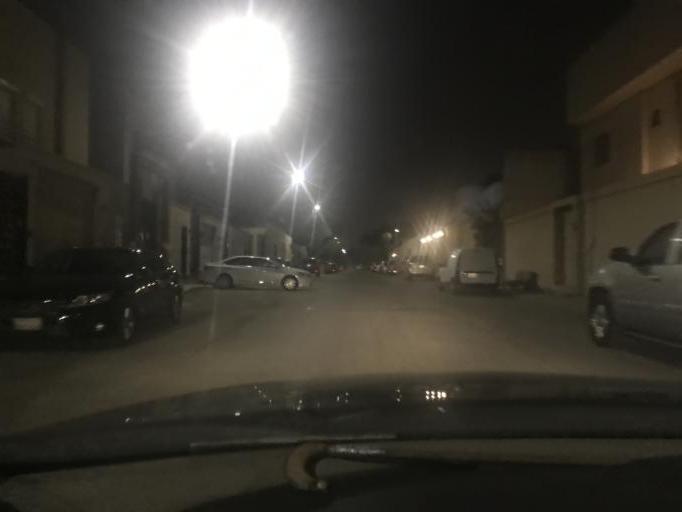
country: SA
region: Ar Riyad
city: Riyadh
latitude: 24.7263
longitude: 46.7646
